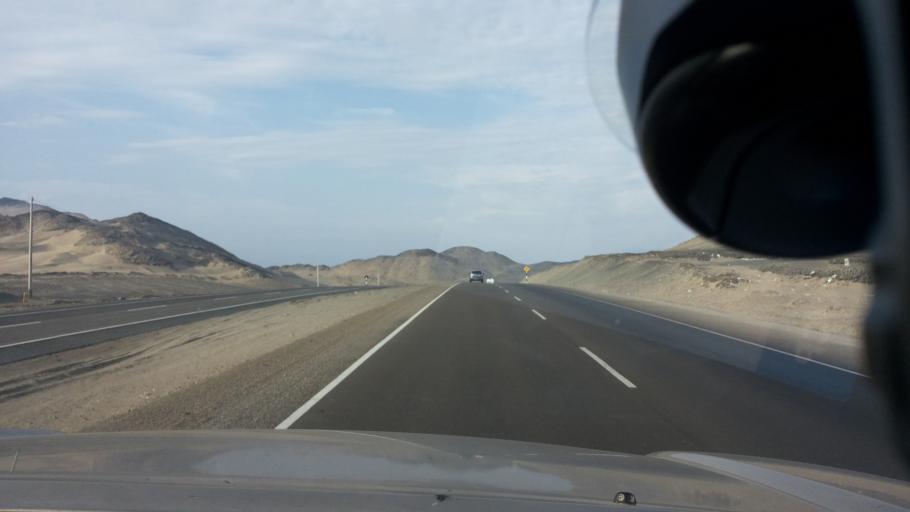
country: PE
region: Ancash
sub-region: Provincia de Casma
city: Casma
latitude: -9.6643
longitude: -78.2693
